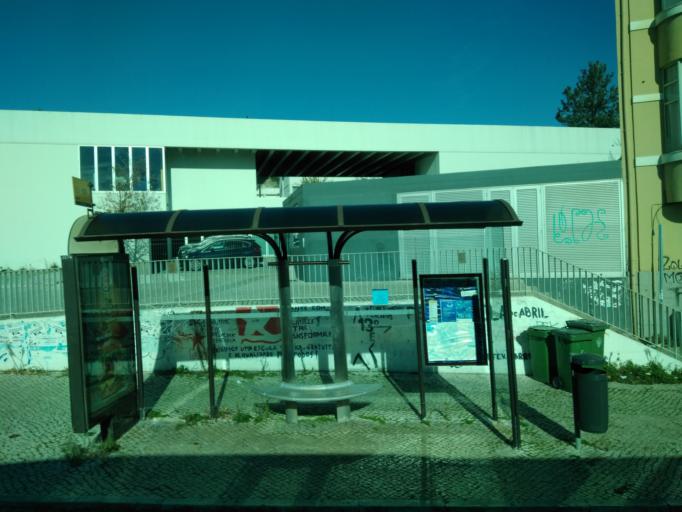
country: PT
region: Lisbon
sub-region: Lisbon
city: Lisbon
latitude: 38.7413
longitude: -9.1630
